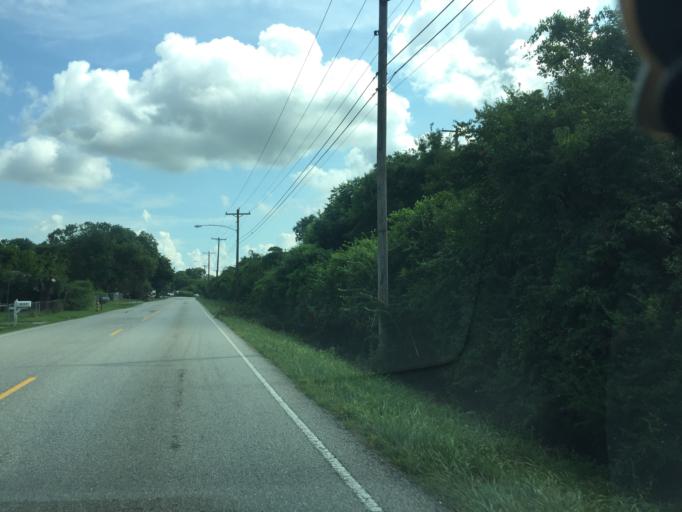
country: US
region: Tennessee
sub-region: Hamilton County
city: East Chattanooga
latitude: 35.0664
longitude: -85.2665
